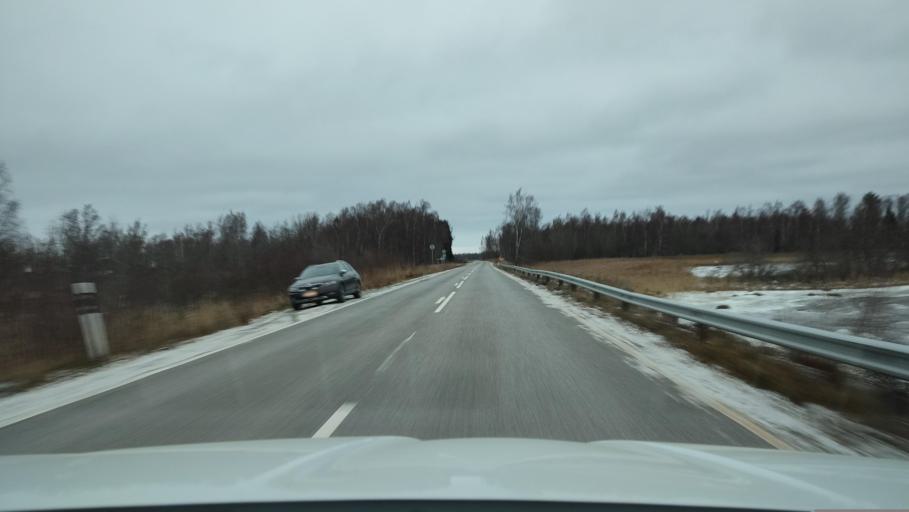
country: FI
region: Ostrobothnia
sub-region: Vaasa
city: Replot
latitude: 63.2773
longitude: 21.3422
